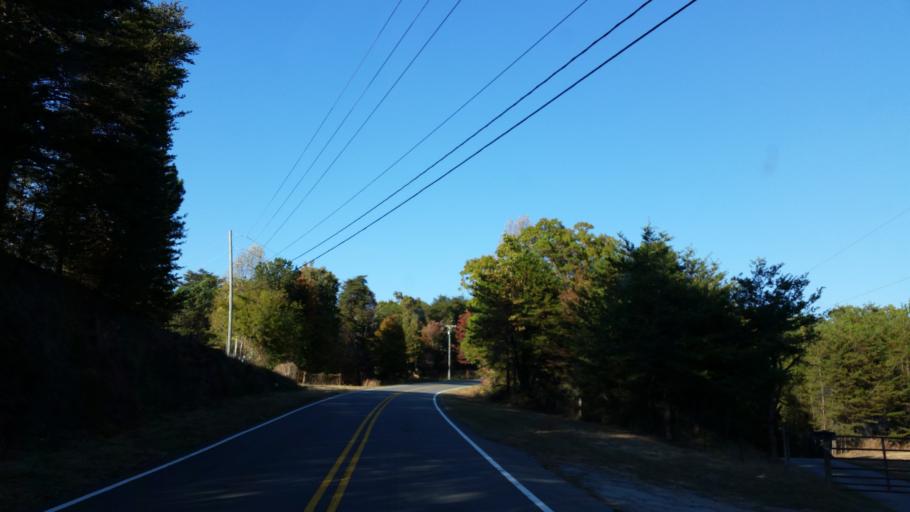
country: US
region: Georgia
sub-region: Pickens County
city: Jasper
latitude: 34.5417
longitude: -84.4751
